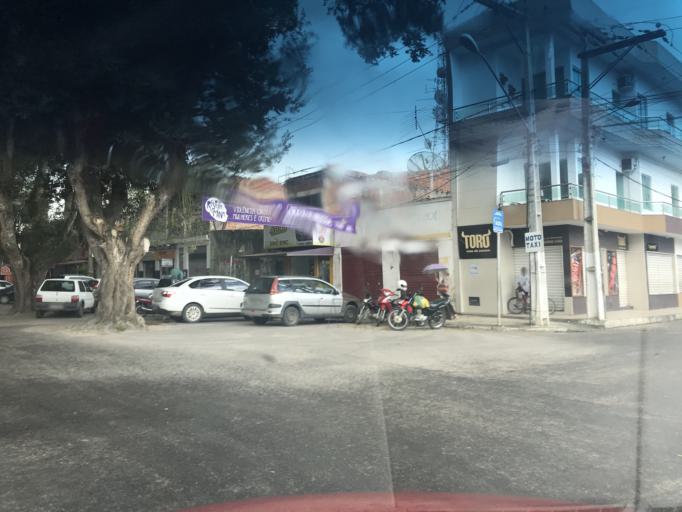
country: BR
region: Bahia
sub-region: Cruz Das Almas
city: Cruz das Almas
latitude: -12.6724
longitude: -39.1006
